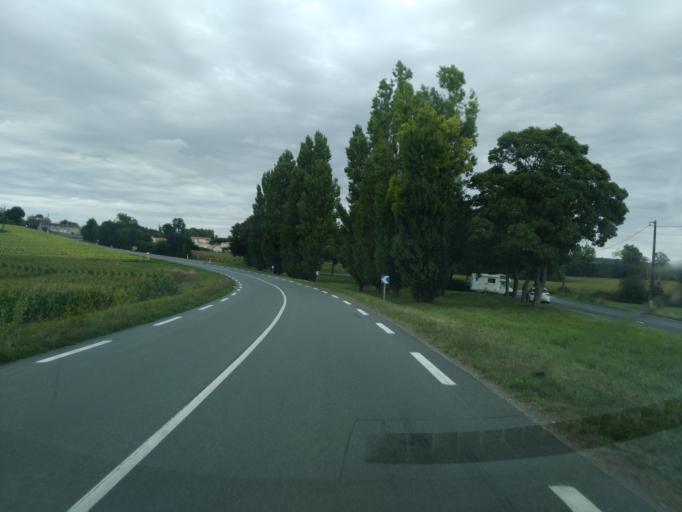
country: FR
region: Poitou-Charentes
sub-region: Departement de la Charente-Maritime
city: Pons
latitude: 45.5912
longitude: -0.5219
